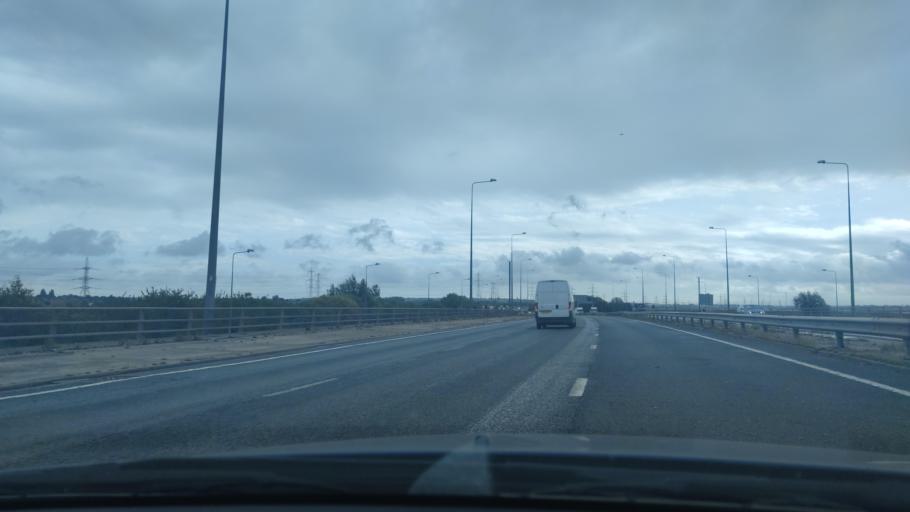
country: GB
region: England
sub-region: Greater London
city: Erith
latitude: 51.5117
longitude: 0.1857
